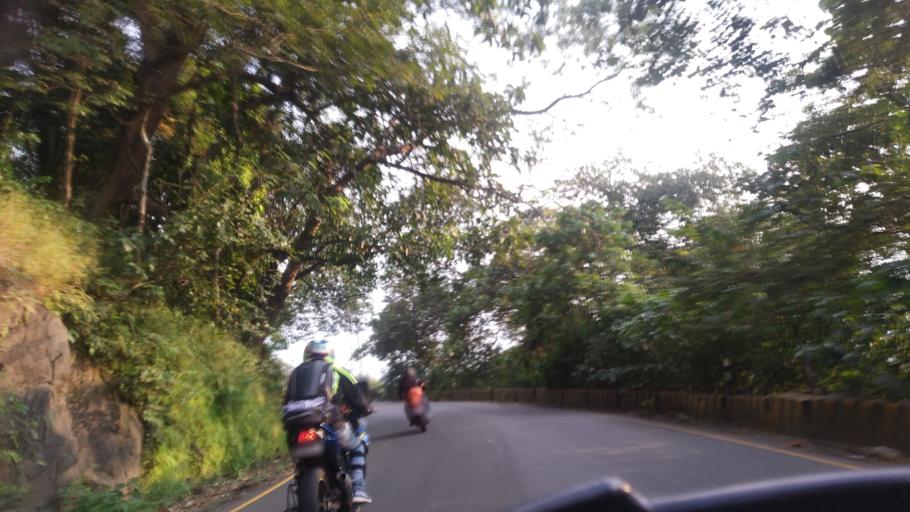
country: IN
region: Kerala
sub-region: Wayanad
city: Kalpetta
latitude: 11.5126
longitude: 76.0151
